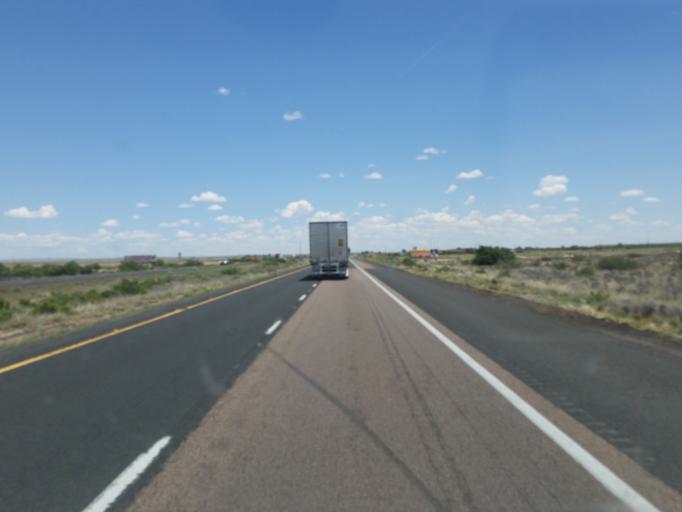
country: US
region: Arizona
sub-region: Navajo County
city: Joseph City
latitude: 34.9700
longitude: -110.4470
